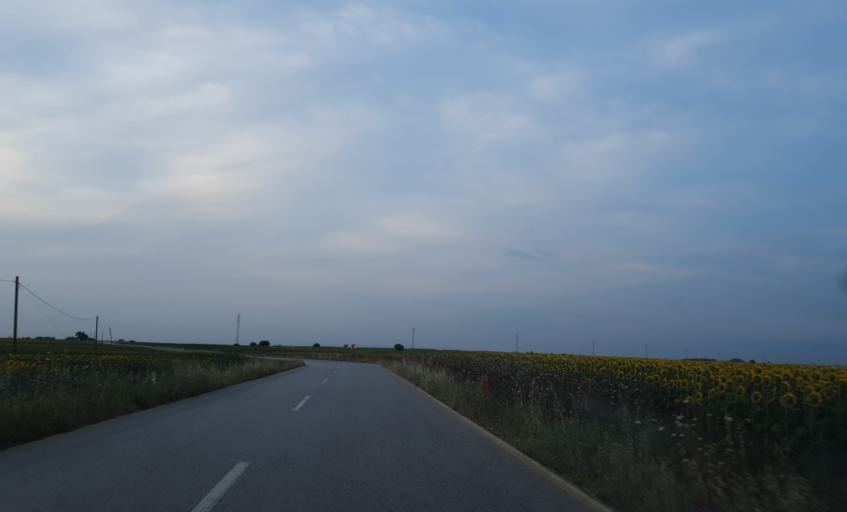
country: TR
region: Kirklareli
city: Buyukkaristiran
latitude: 41.3274
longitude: 27.6067
